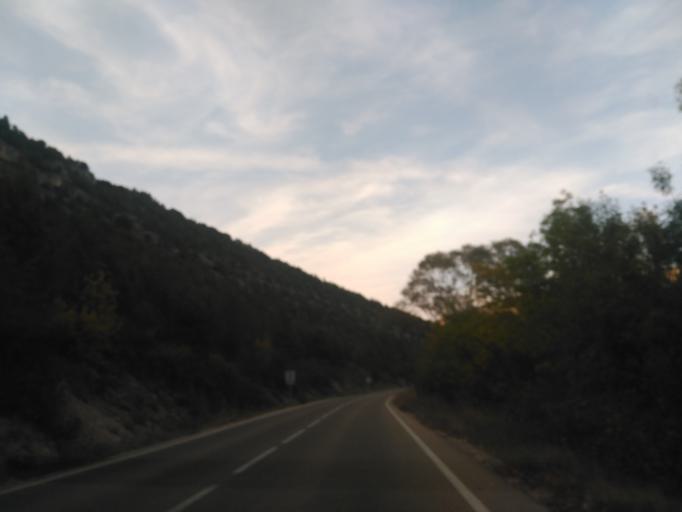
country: ES
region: Castille and Leon
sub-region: Provincia de Soria
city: Ucero
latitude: 41.7263
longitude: -3.0488
